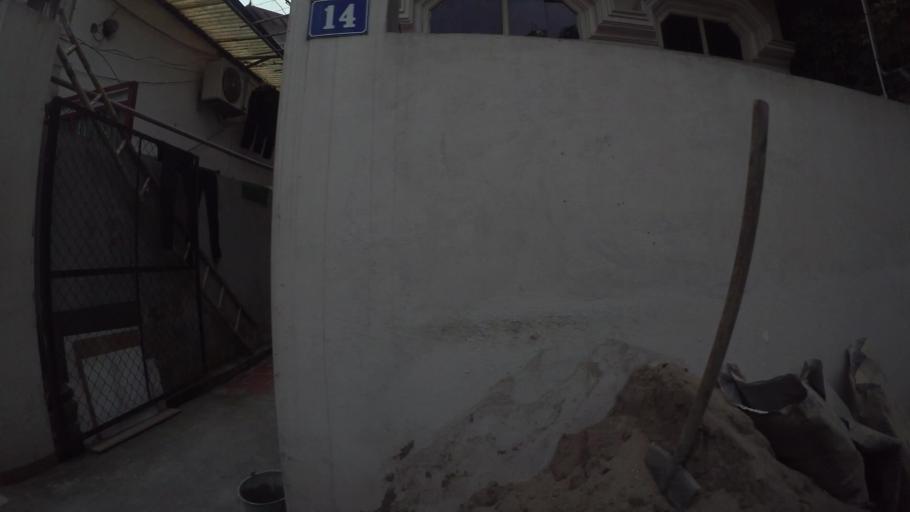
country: VN
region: Ha Noi
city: Trau Quy
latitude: 21.0533
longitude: 105.9024
